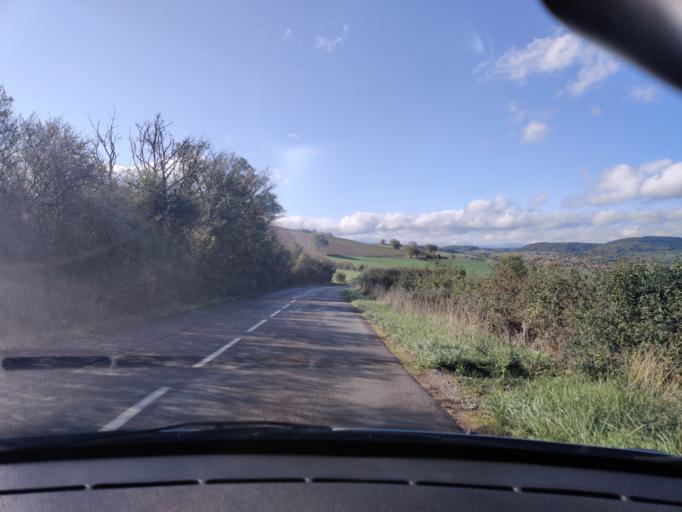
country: FR
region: Auvergne
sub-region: Departement du Puy-de-Dome
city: Combronde
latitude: 45.9884
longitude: 3.1174
